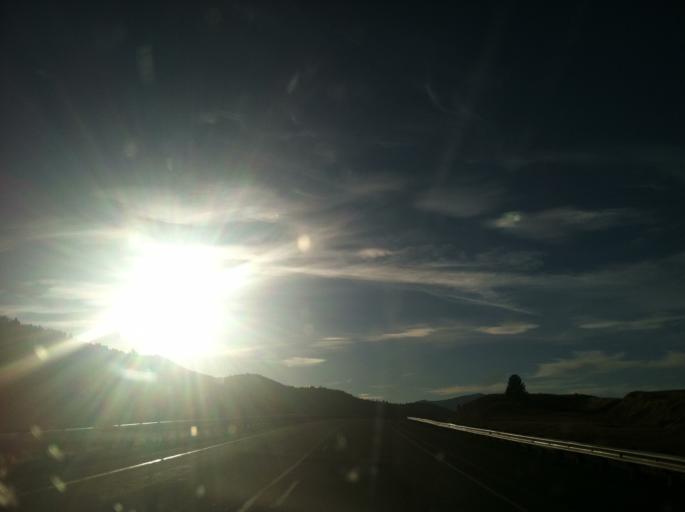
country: US
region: Montana
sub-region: Granite County
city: Philipsburg
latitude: 46.6971
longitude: -113.2276
